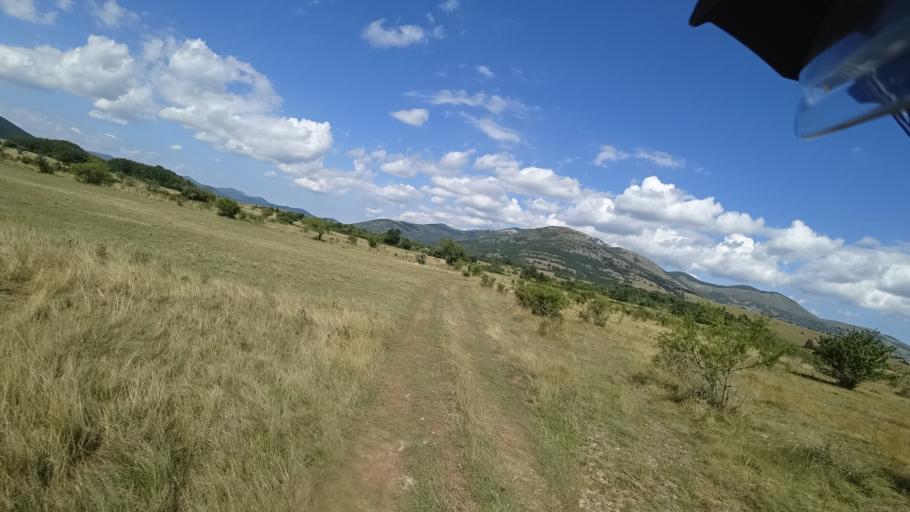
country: HR
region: Zadarska
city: Gracac
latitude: 44.4196
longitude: 15.9210
